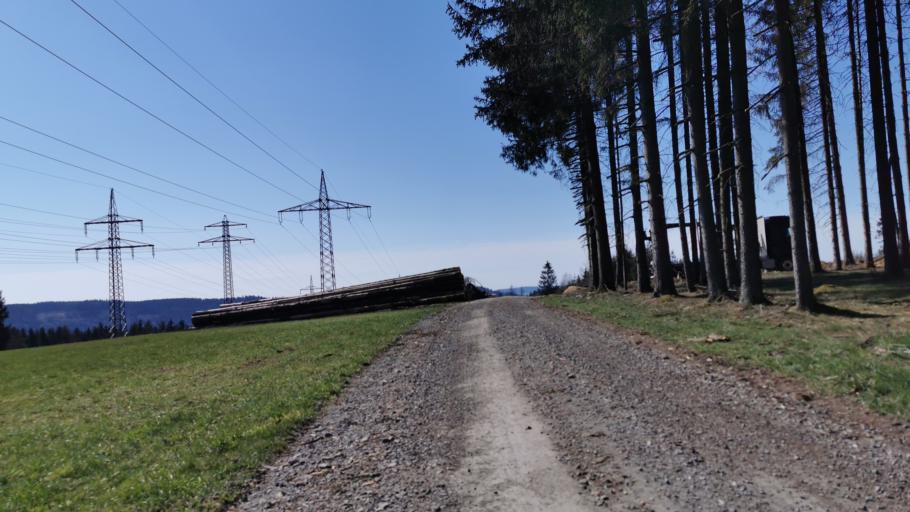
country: DE
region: Bavaria
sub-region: Upper Franconia
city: Teuschnitz
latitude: 50.3970
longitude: 11.3337
